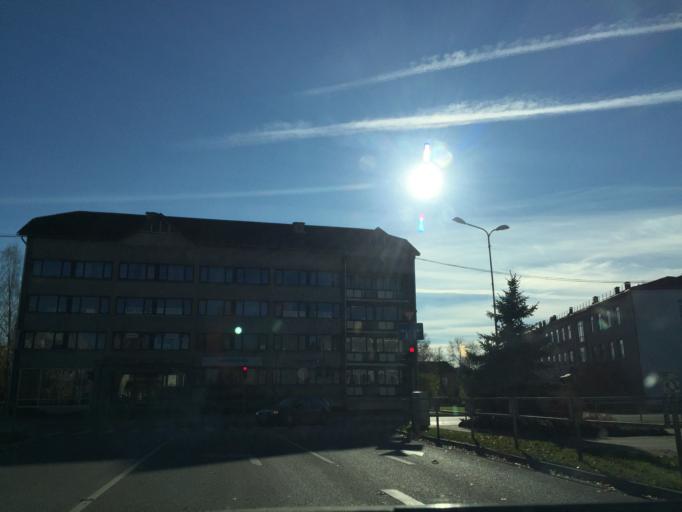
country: LV
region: Aizkraukles Rajons
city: Aizkraukle
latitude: 56.6010
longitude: 25.2549
